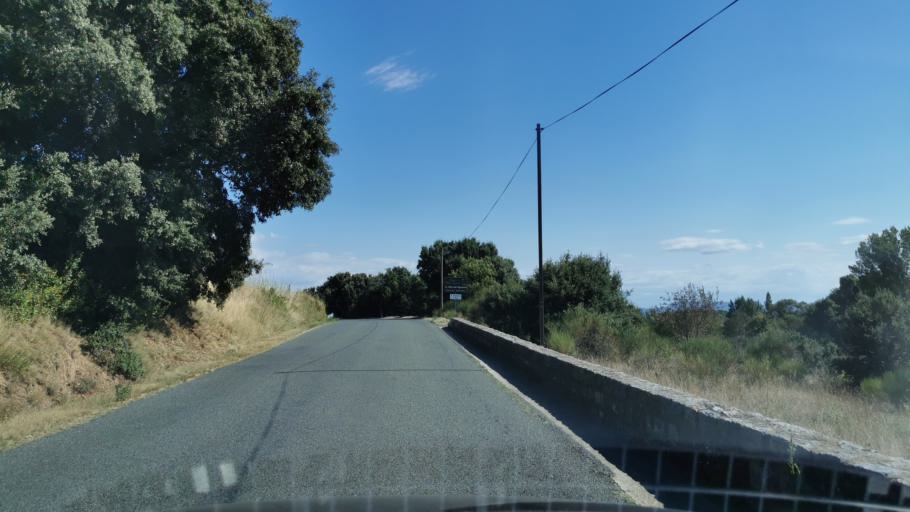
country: FR
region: Languedoc-Roussillon
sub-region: Departement de l'Aude
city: Caunes-Minervois
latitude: 43.3151
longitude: 2.5493
